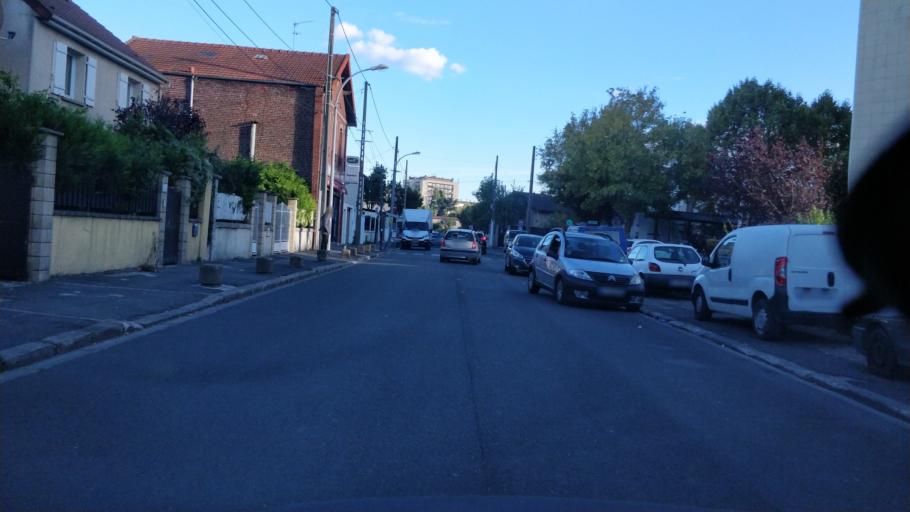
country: FR
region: Ile-de-France
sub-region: Departement de Seine-Saint-Denis
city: Bondy
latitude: 48.8916
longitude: 2.4901
